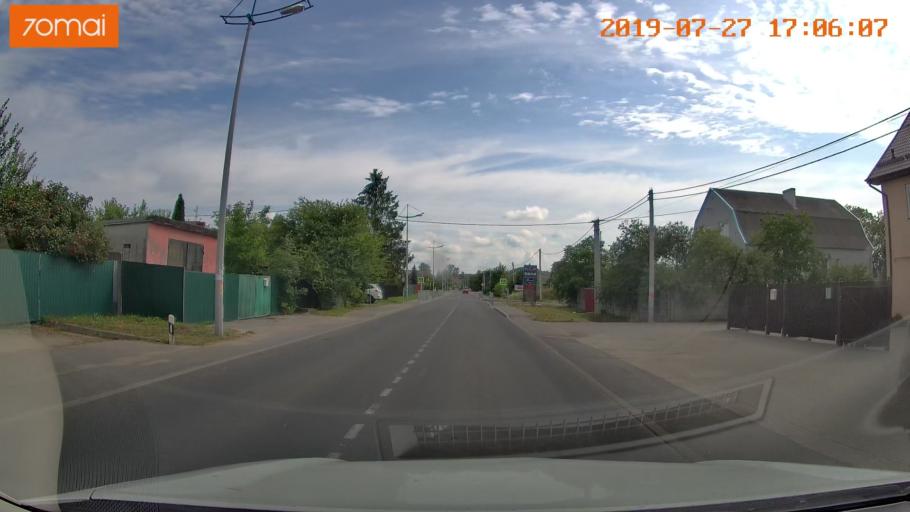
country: RU
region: Kaliningrad
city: Bol'shoe Isakovo
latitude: 54.7236
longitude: 20.6005
